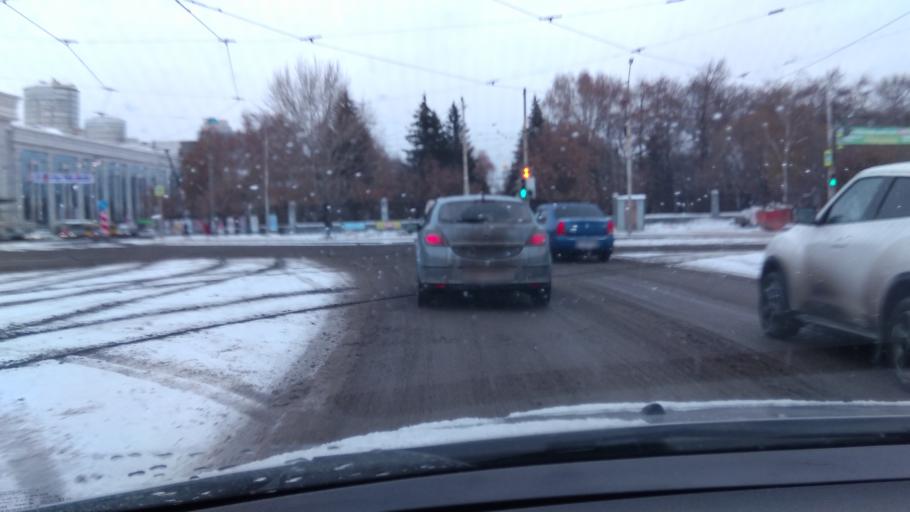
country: RU
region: Sverdlovsk
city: Yekaterinburg
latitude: 56.8269
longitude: 60.6034
